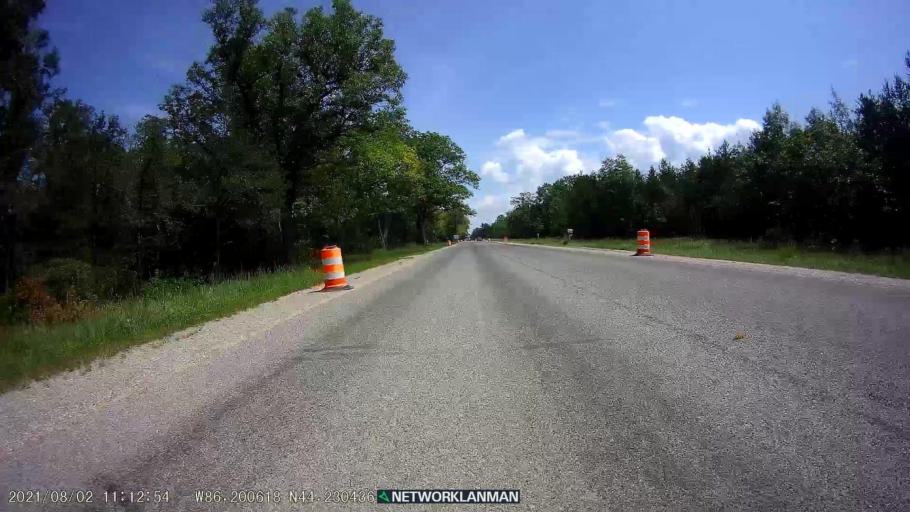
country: US
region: Michigan
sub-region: Manistee County
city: Manistee
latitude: 44.2306
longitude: -86.2009
